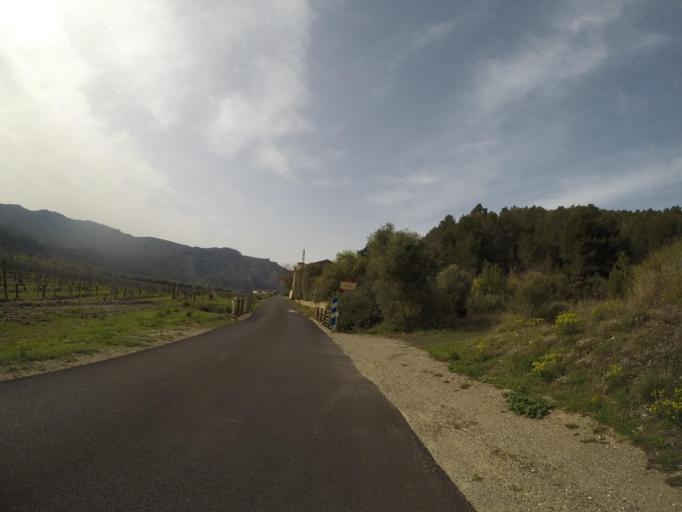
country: FR
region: Languedoc-Roussillon
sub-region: Departement des Pyrenees-Orientales
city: Baixas
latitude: 42.7834
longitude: 2.7668
